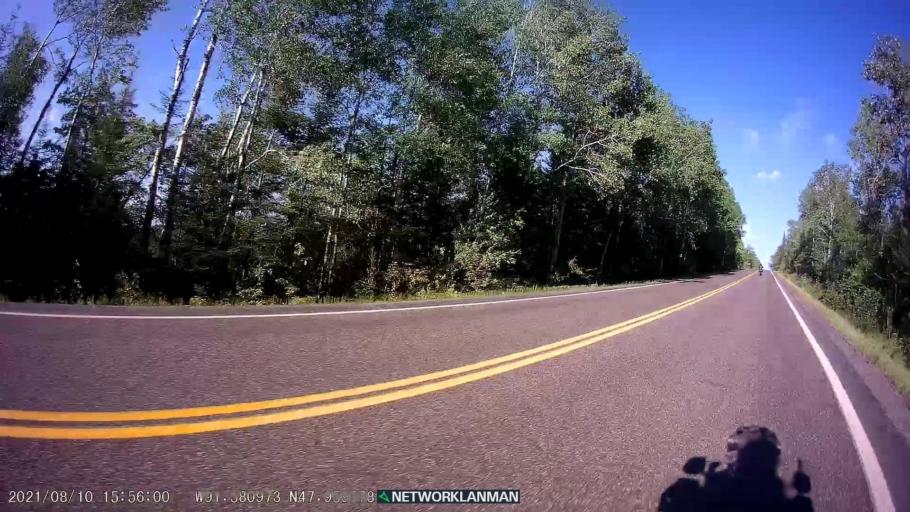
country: US
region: Minnesota
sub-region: Saint Louis County
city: Ely
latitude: 47.9596
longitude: -91.5805
